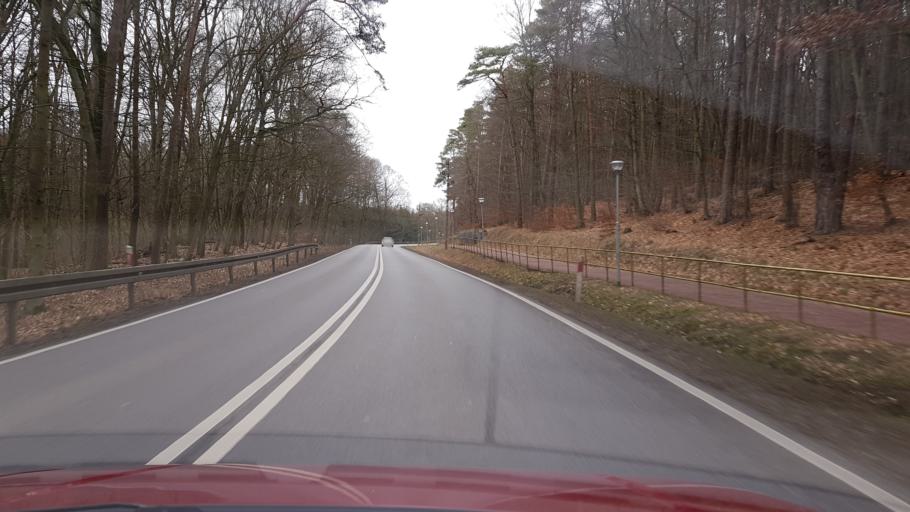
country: PL
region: West Pomeranian Voivodeship
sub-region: Szczecin
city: Szczecin
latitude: 53.4865
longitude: 14.4838
